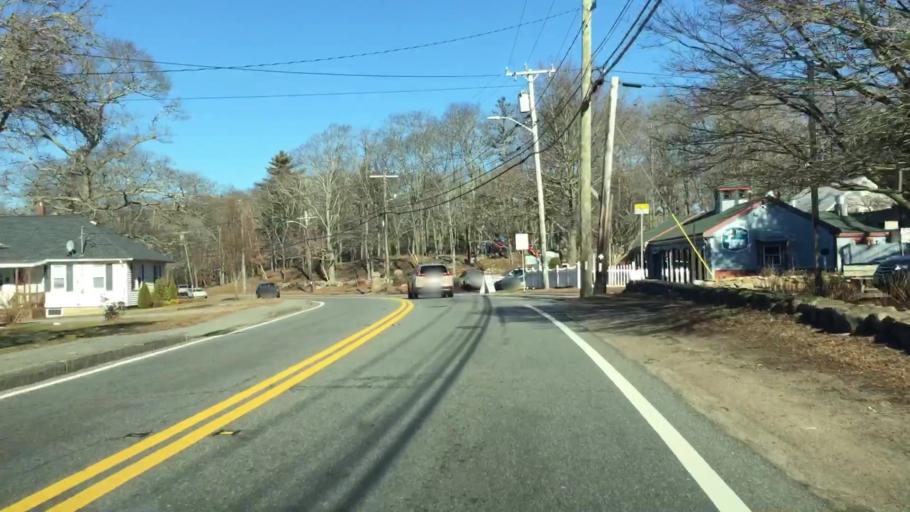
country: US
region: Massachusetts
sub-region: Barnstable County
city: Falmouth
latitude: 41.5672
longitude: -70.6174
